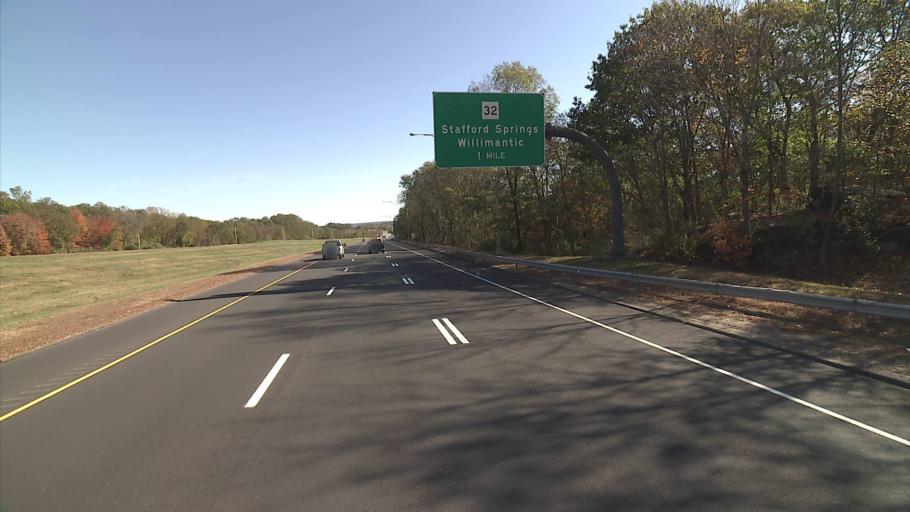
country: US
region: Connecticut
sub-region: Tolland County
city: Mansfield City
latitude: 41.7223
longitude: -72.2636
